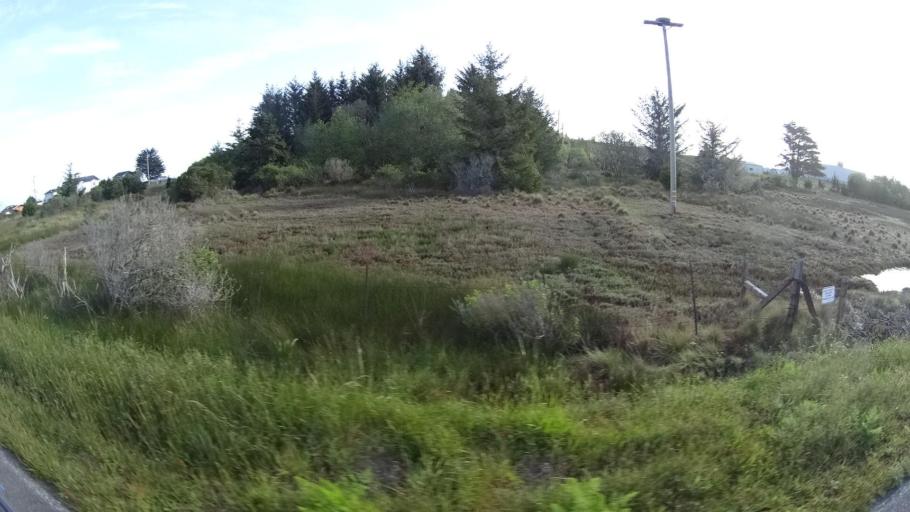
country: US
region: California
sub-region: Humboldt County
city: Humboldt Hill
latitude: 40.7399
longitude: -124.2142
